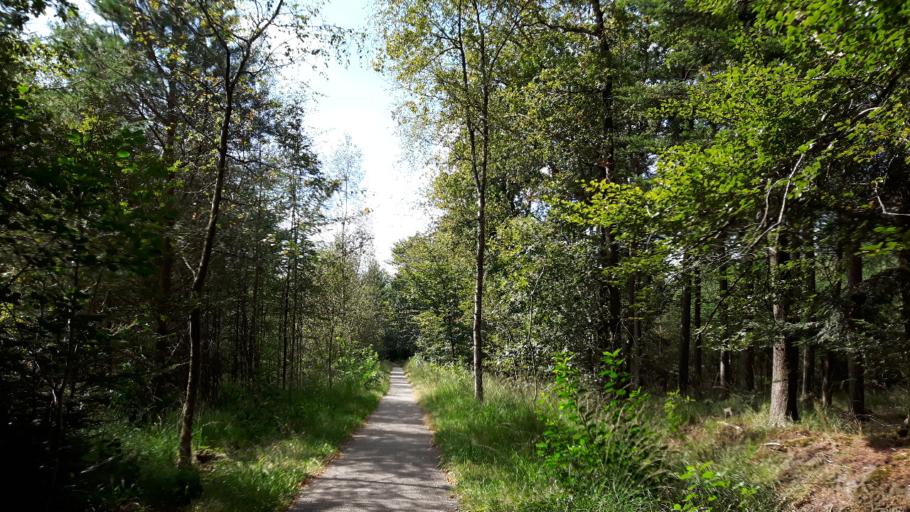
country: NL
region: Friesland
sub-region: Gemeente Smallingerland
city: Drachtstercompagnie
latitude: 53.0829
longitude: 6.2314
